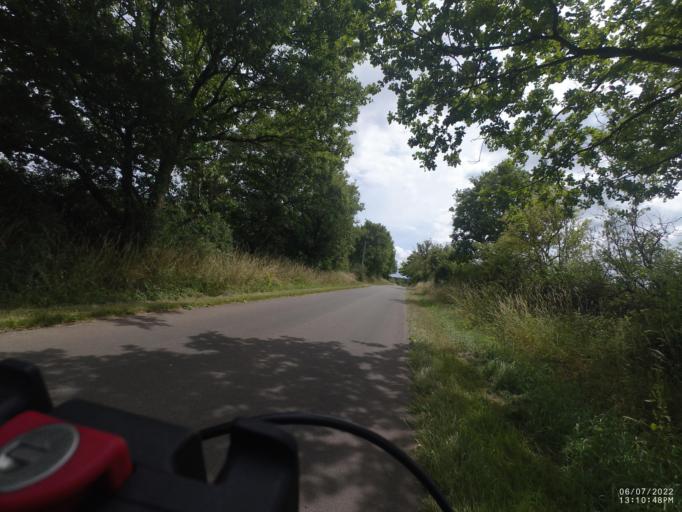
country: DE
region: Rheinland-Pfalz
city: Densborn
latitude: 50.1244
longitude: 6.6070
